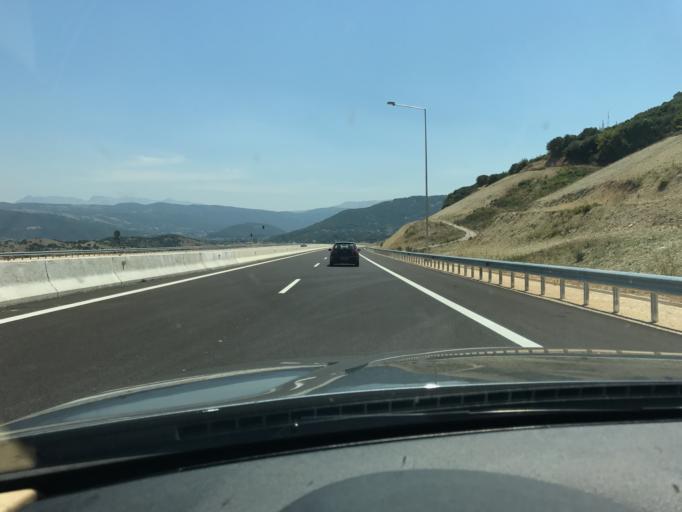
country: GR
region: Epirus
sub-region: Nomos Ioanninon
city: Pedini
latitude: 39.5599
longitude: 20.8308
